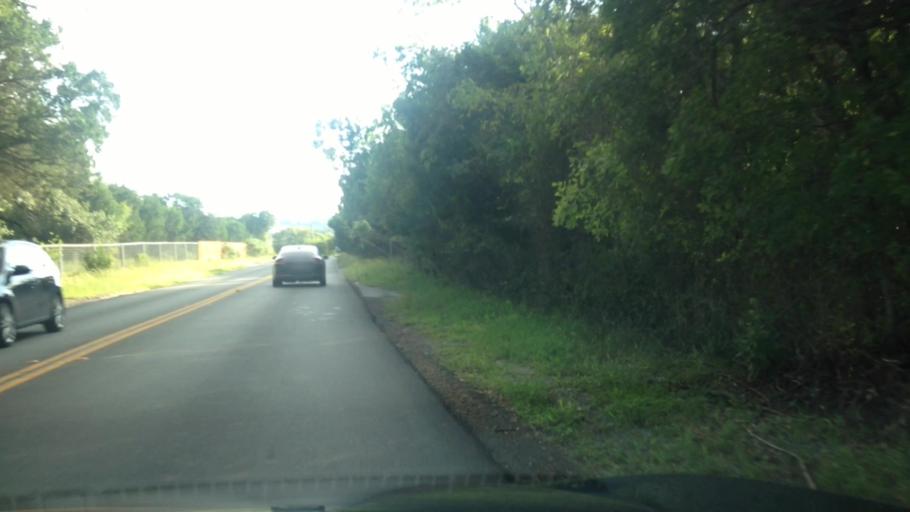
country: US
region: Texas
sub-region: Bexar County
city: Cross Mountain
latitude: 29.6323
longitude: -98.6029
